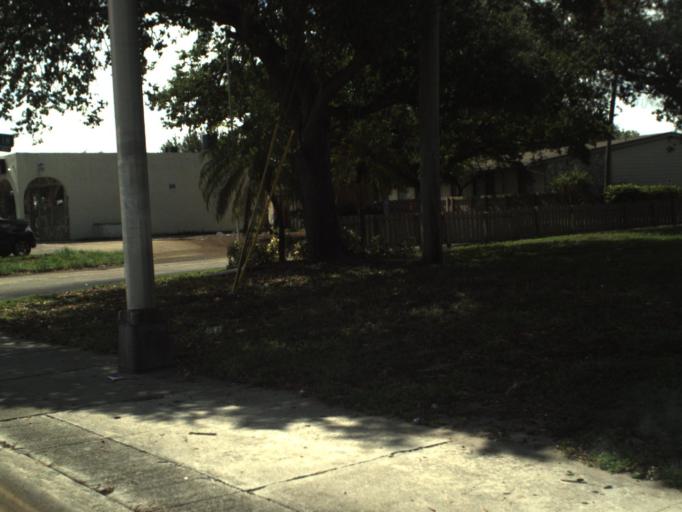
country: US
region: Florida
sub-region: Broward County
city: Dania Beach
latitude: 26.0335
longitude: -80.1573
